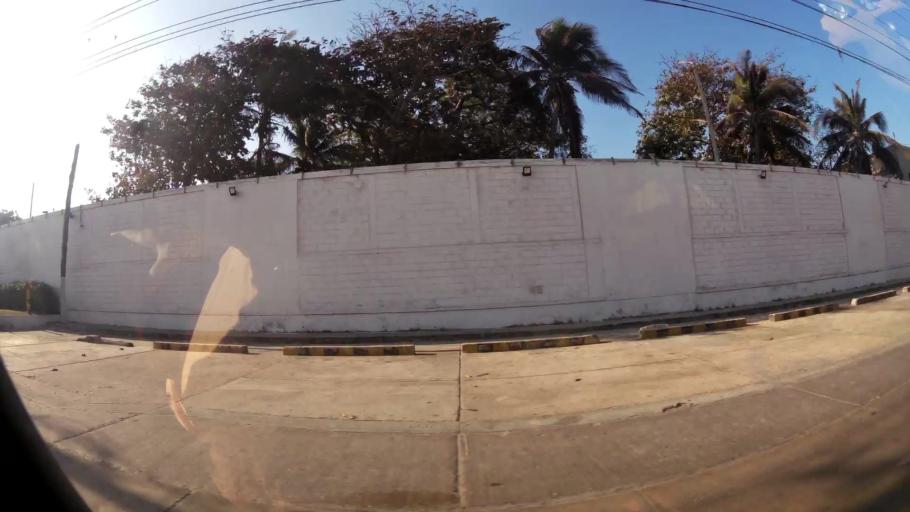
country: CO
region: Atlantico
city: Barranquilla
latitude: 11.0386
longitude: -74.8221
